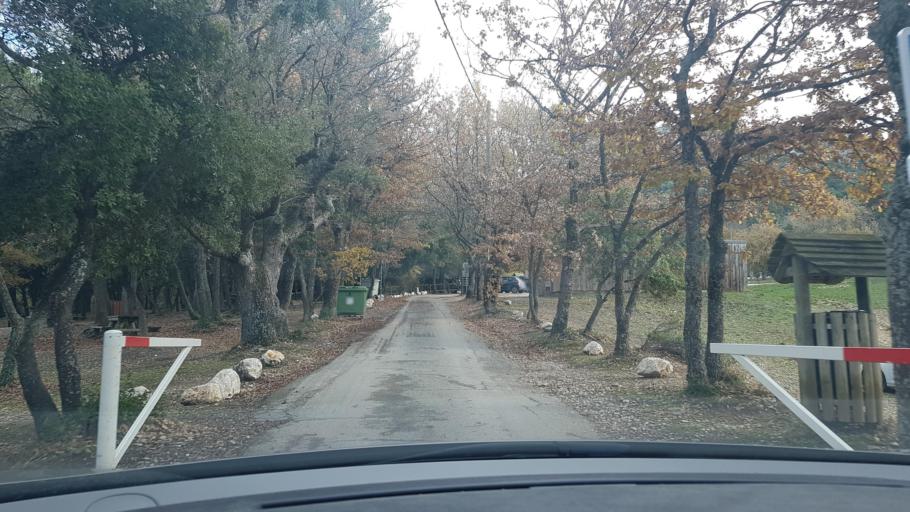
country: FR
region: Provence-Alpes-Cote d'Azur
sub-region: Departement des Bouches-du-Rhone
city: Mimet
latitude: 43.4136
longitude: 5.4716
